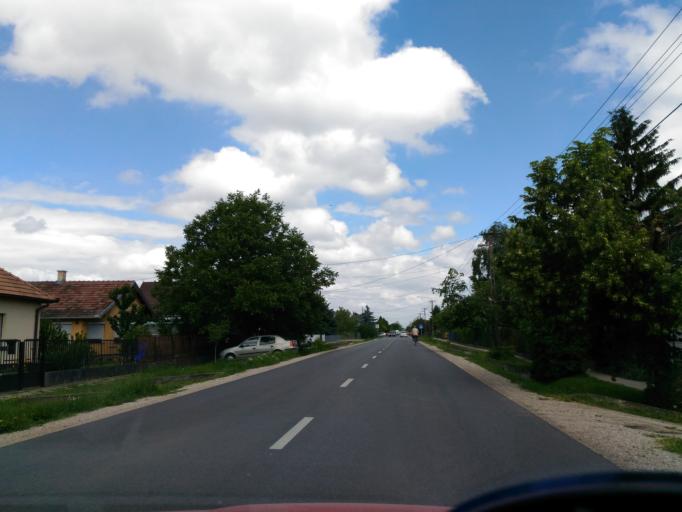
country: HU
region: Fejer
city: Pusztaszabolcs
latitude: 47.1400
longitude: 18.7582
